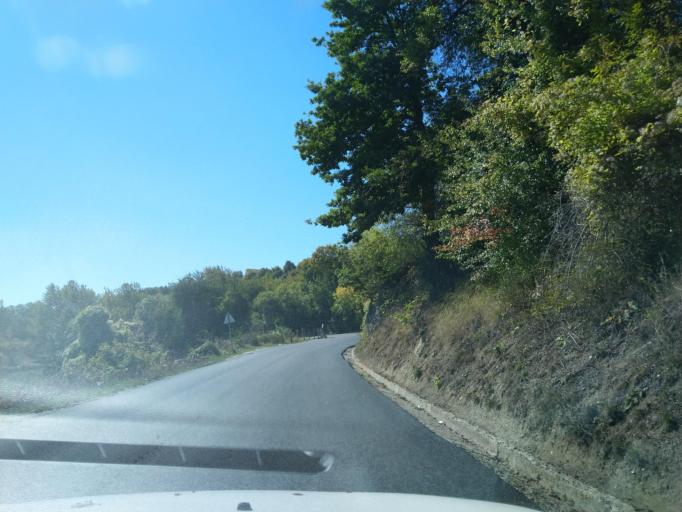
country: RS
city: Sokolovica
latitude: 43.2572
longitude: 20.2307
